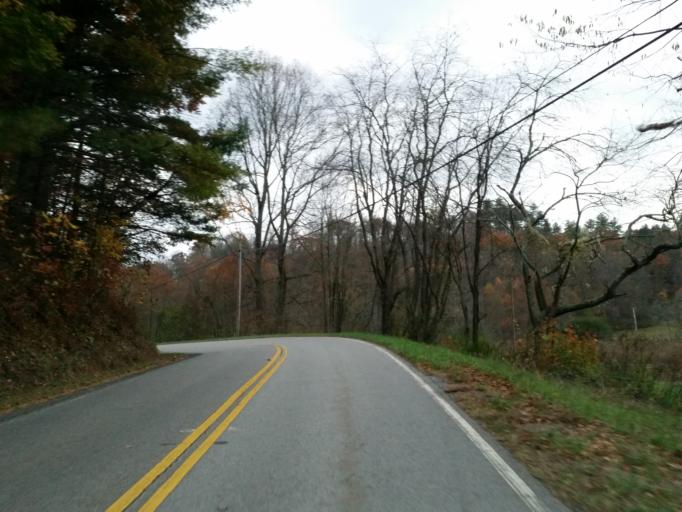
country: US
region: Georgia
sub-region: Union County
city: Blairsville
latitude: 34.7184
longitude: -84.0668
